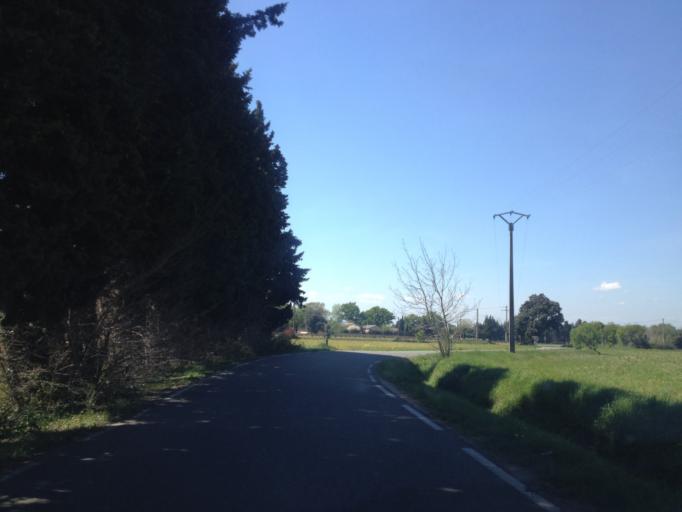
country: FR
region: Provence-Alpes-Cote d'Azur
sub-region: Departement du Vaucluse
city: Orange
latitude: 44.1106
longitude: 4.8015
